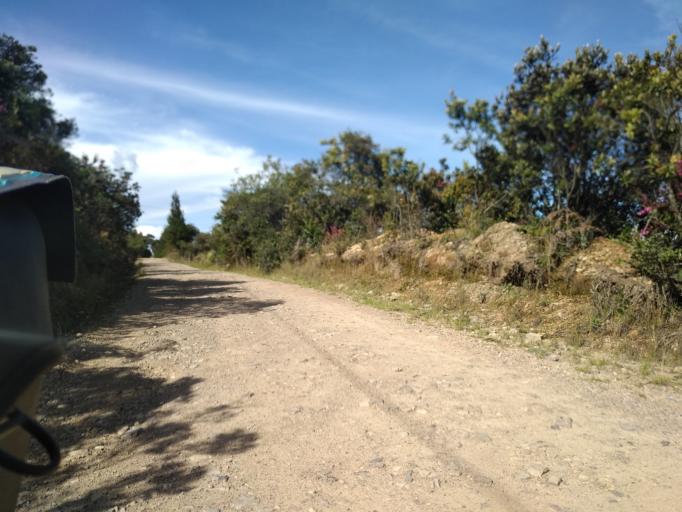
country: CO
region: Cundinamarca
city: Guacheta
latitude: 5.4559
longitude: -73.6465
